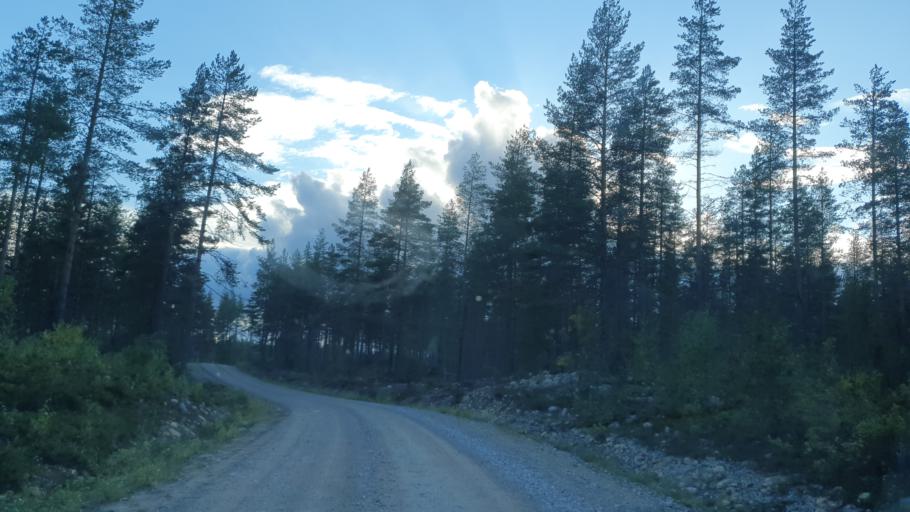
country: FI
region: Kainuu
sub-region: Kehys-Kainuu
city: Kuhmo
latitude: 64.3363
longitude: 29.9458
